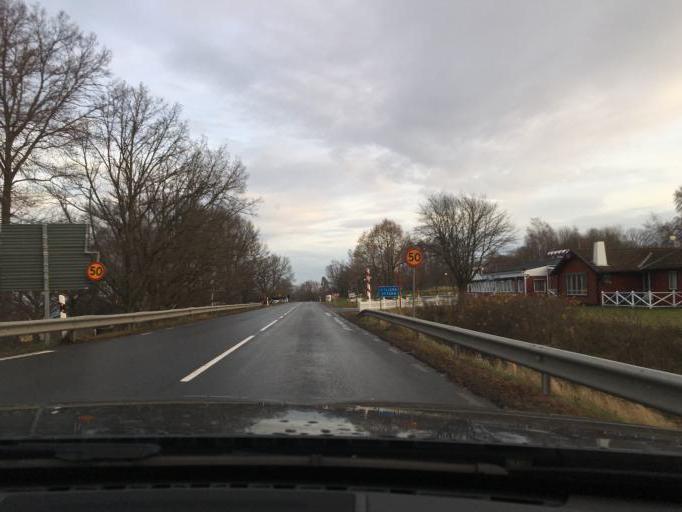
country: SE
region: Joenkoeping
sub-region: Jonkopings Kommun
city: Graenna
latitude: 57.9942
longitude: 14.4394
